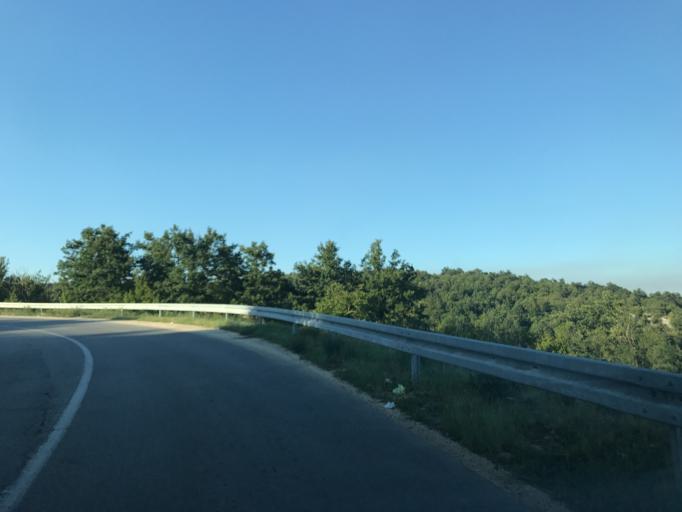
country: RO
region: Mehedinti
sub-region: Comuna Svinita
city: Svinita
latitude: 44.3011
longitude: 22.2597
